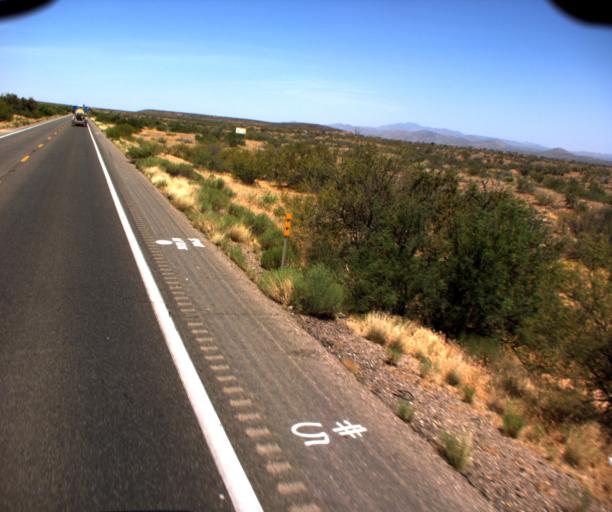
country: US
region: Arizona
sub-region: Gila County
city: Peridot
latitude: 33.3153
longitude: -110.5201
